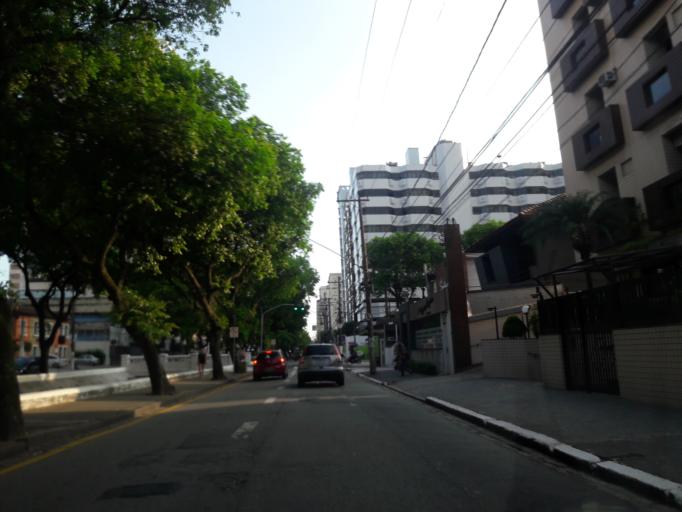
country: BR
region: Sao Paulo
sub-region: Santos
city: Santos
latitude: -23.9634
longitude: -46.3386
